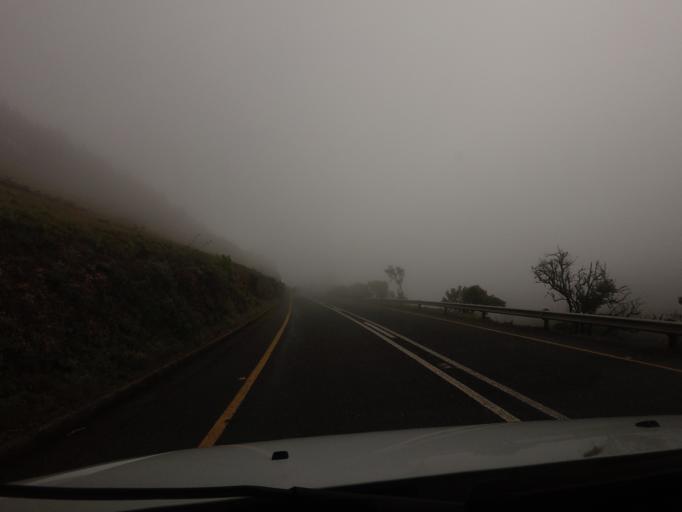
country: ZA
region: Mpumalanga
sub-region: Ehlanzeni District
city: Lydenburg
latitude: -25.1660
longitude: 30.6371
